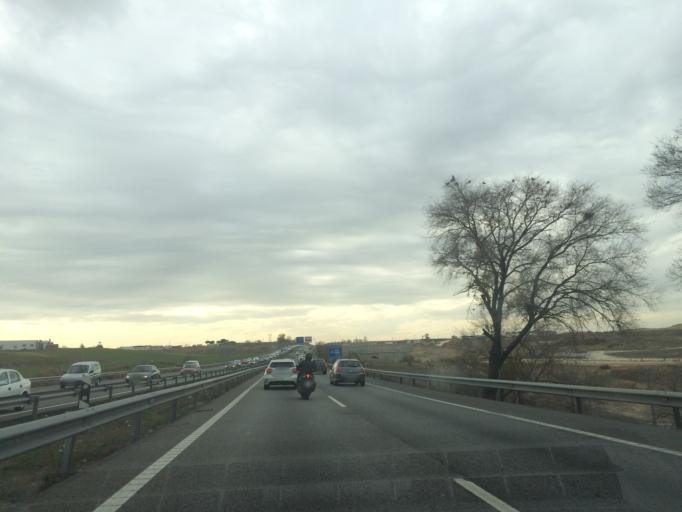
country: ES
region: Madrid
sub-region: Provincia de Madrid
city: Mostoles
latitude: 40.3124
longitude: -3.9002
